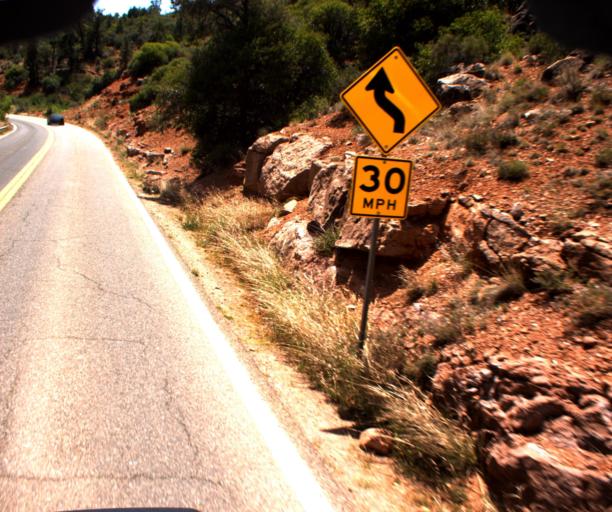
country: US
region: Arizona
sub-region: Coconino County
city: Sedona
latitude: 34.8913
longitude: -111.7342
